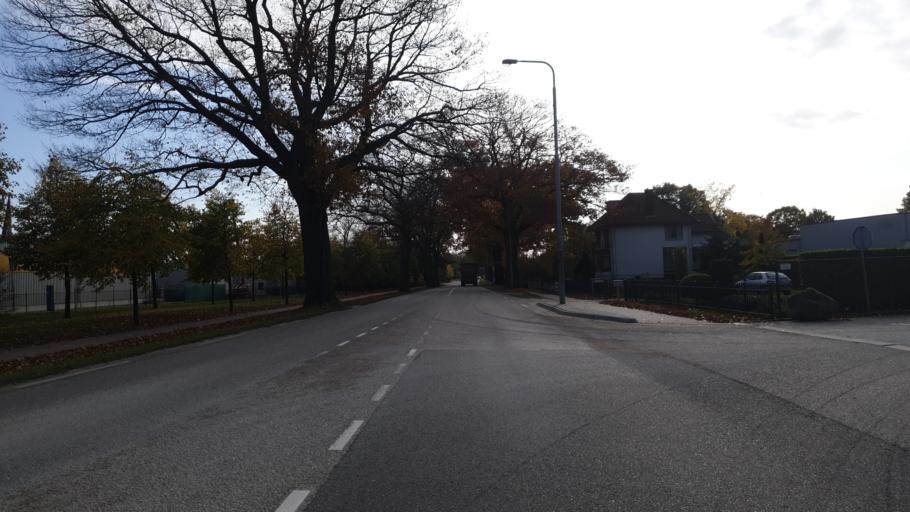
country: NL
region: Limburg
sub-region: Gemeente Gennep
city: Gennep
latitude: 51.6814
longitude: 5.9747
